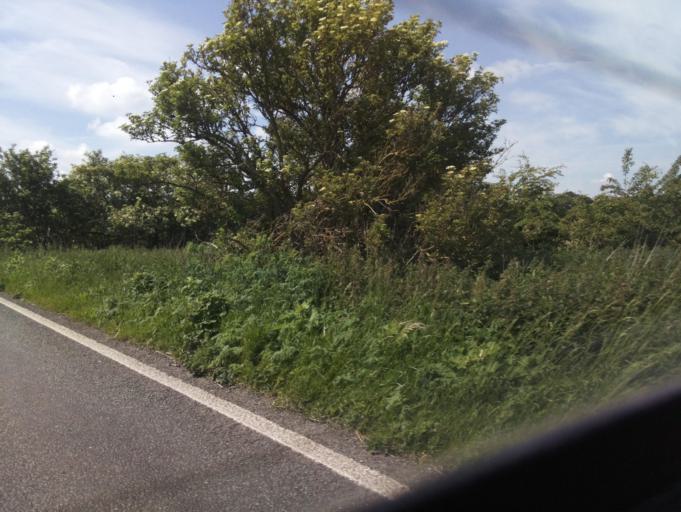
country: GB
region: England
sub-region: Lincolnshire
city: Burton
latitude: 53.3648
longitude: -0.5454
